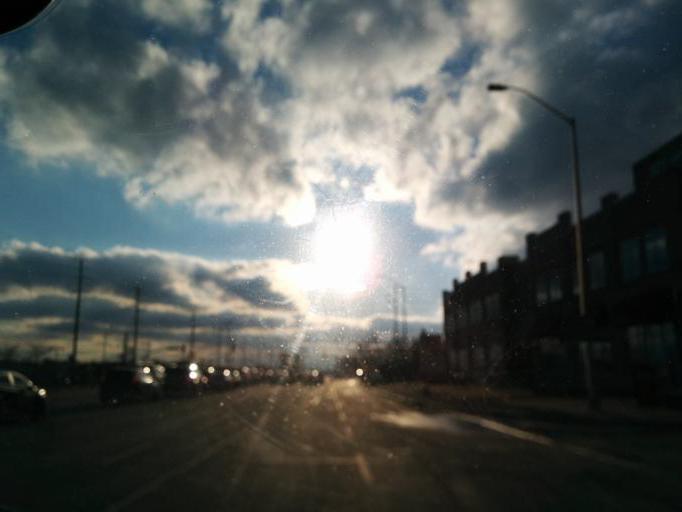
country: CA
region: Ontario
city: Oakville
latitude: 43.4658
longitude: -79.7442
